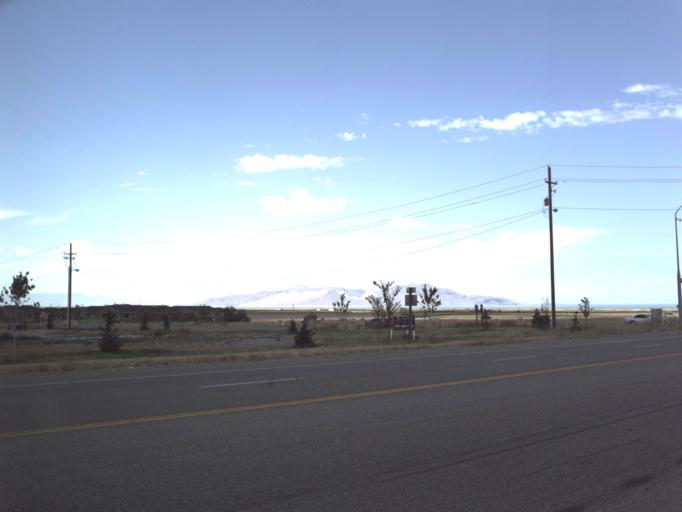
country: US
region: Utah
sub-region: Tooele County
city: Stansbury park
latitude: 40.6482
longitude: -112.2885
